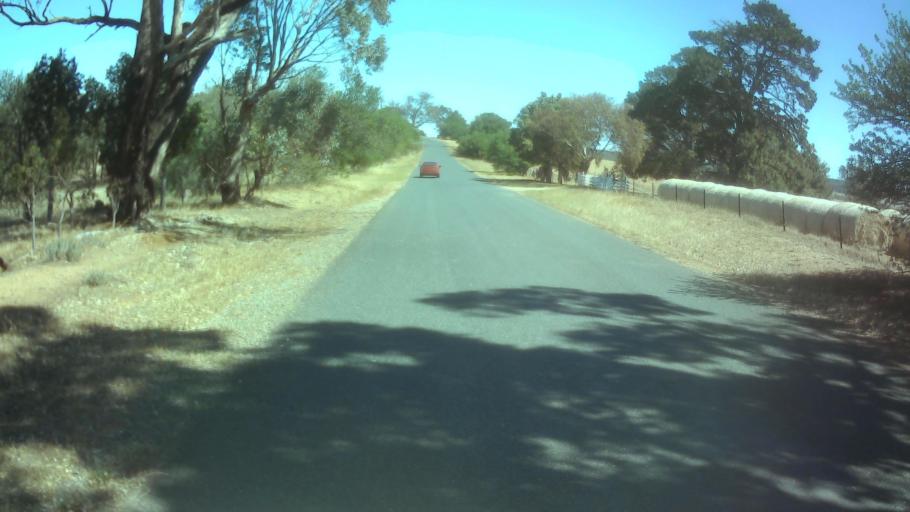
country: AU
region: New South Wales
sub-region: Weddin
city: Grenfell
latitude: -33.9489
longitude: 148.3947
